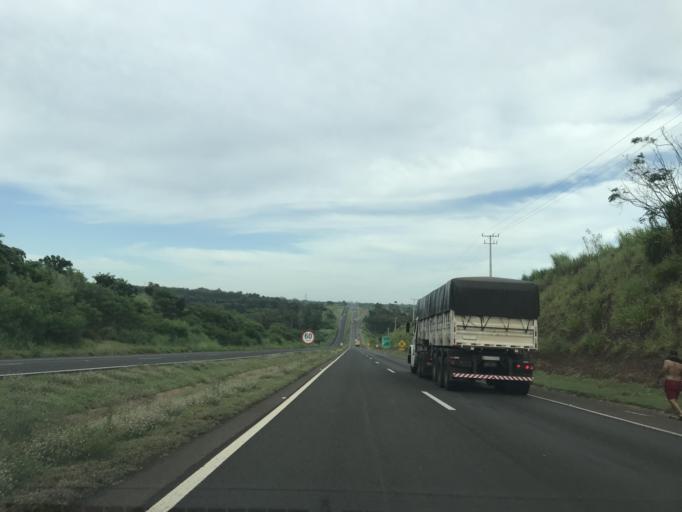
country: BR
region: Parana
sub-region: Alto Parana
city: Alto Parana
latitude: -23.1157
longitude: -52.3257
